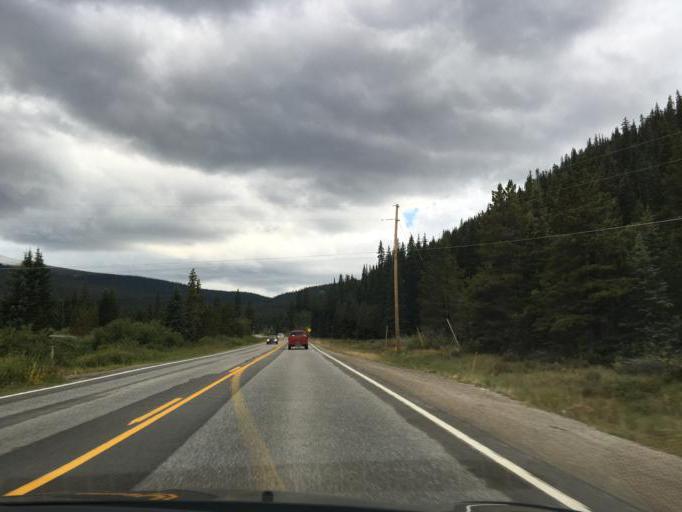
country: US
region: Colorado
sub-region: Summit County
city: Breckenridge
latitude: 39.3983
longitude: -106.0515
